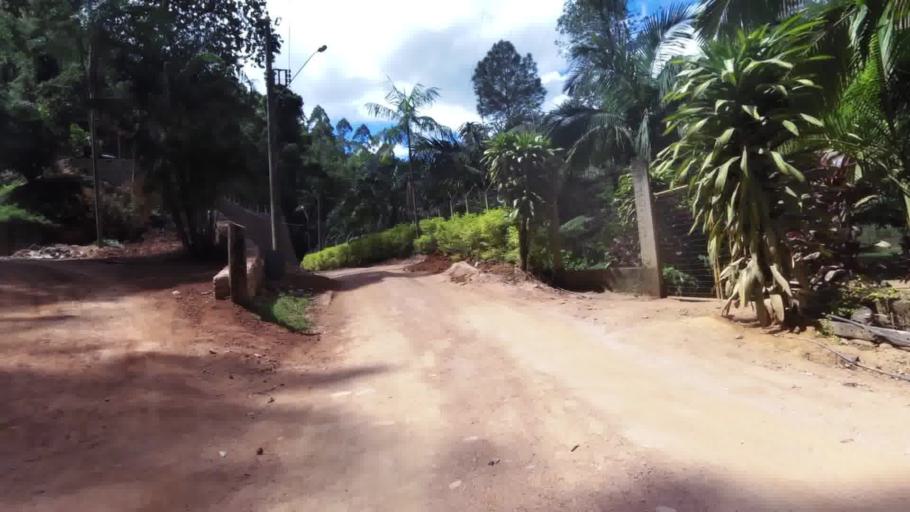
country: BR
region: Espirito Santo
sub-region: Vargem Alta
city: Vargem Alta
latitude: -20.6719
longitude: -40.9994
